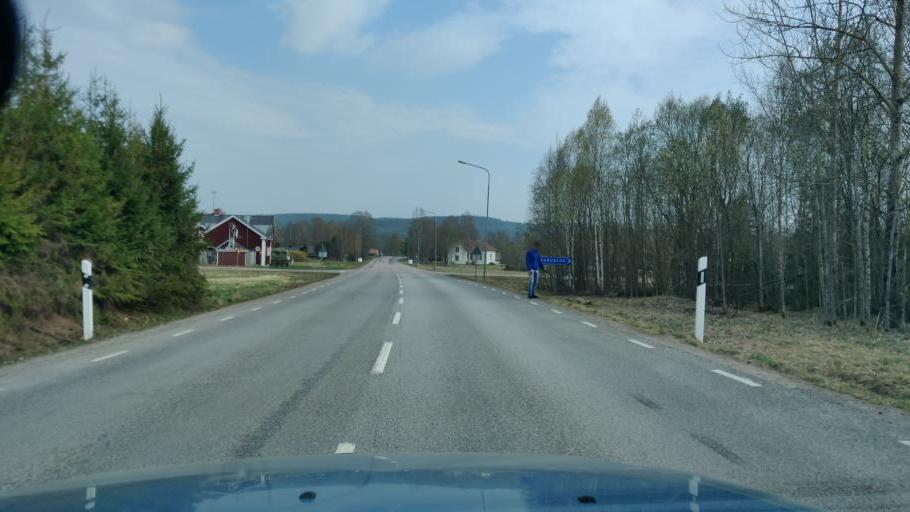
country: SE
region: Vaermland
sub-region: Munkfors Kommun
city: Munkfors
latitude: 59.8319
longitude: 13.5137
